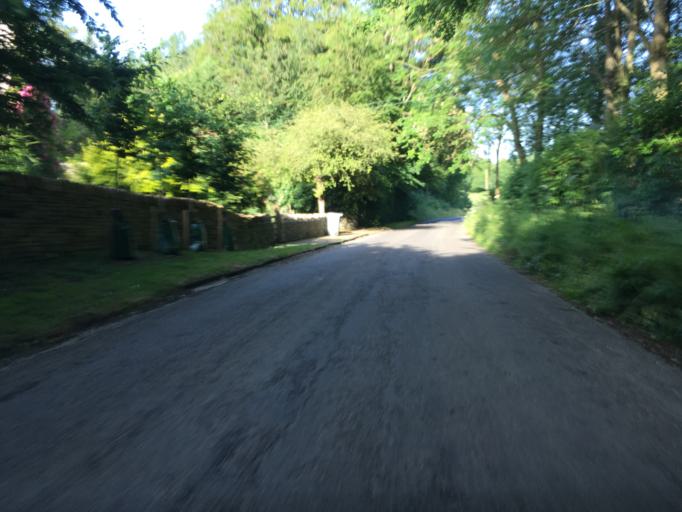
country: GB
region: England
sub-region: Oxfordshire
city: Burford
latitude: 51.8096
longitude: -1.6509
